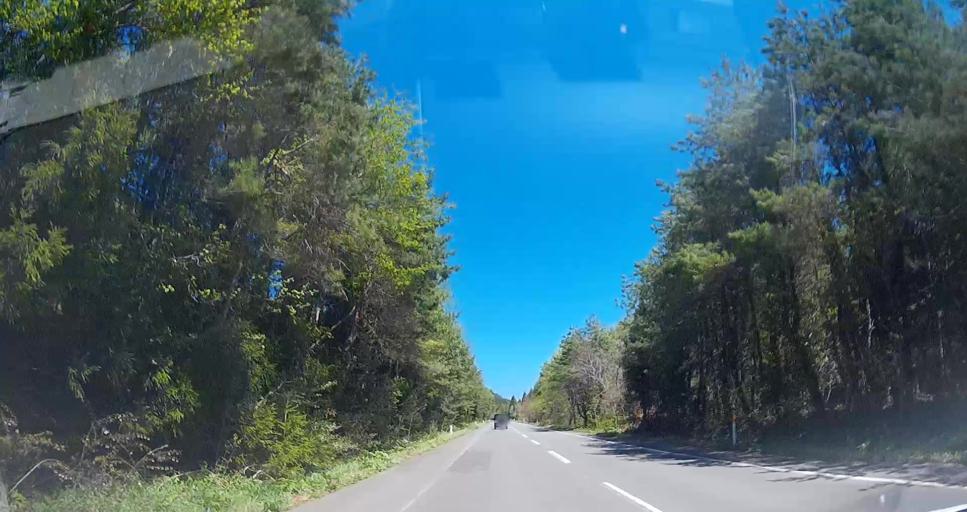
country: JP
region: Aomori
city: Mutsu
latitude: 41.3152
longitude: 141.4006
